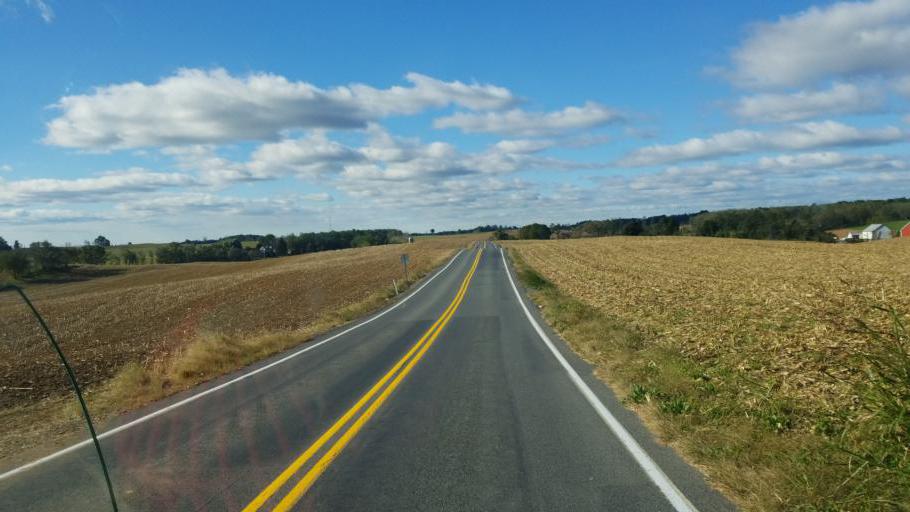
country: US
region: Pennsylvania
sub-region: Franklin County
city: Guilford Siding
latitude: 39.8525
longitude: -77.6053
